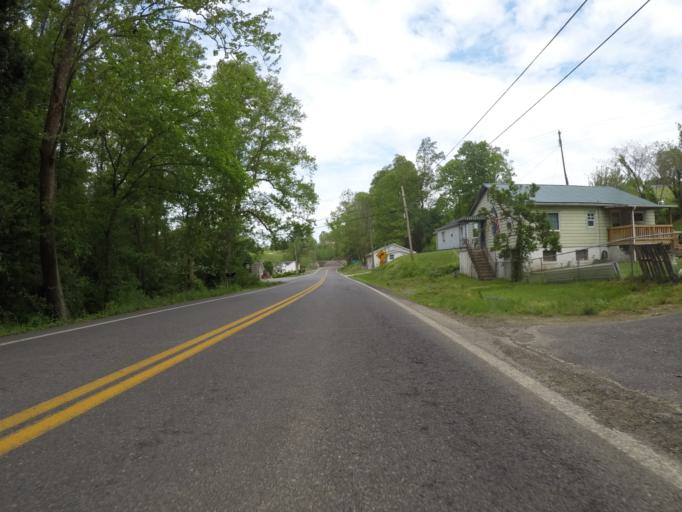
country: US
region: West Virginia
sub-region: Wayne County
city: Ceredo
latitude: 38.3554
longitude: -82.5583
